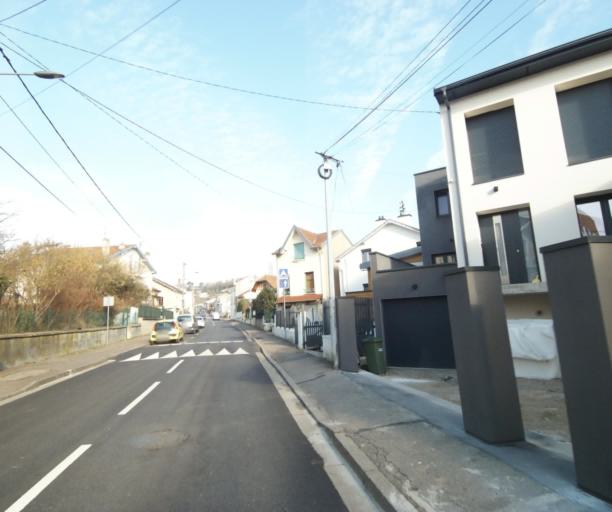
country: FR
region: Lorraine
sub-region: Departement de Meurthe-et-Moselle
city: Laxou
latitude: 48.6826
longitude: 6.1441
